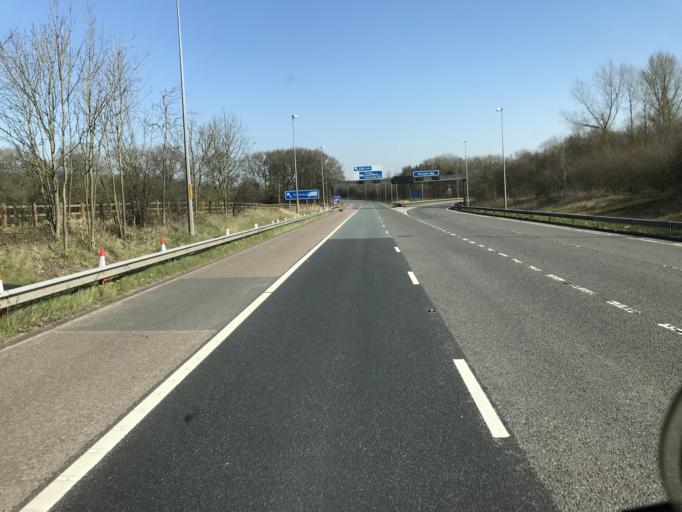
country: GB
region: England
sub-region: Warrington
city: Appleton Thorn
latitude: 53.3511
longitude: -2.5116
